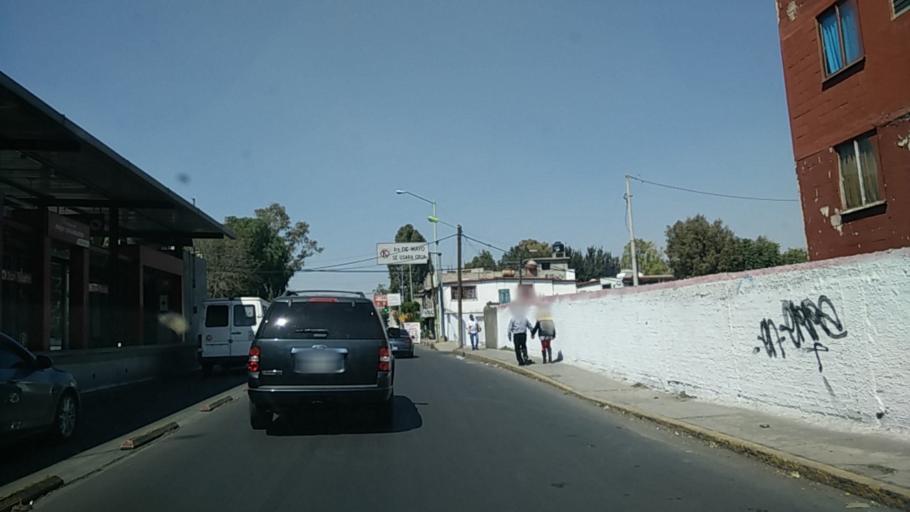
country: MX
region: Mexico
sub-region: Atenco
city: Colonia el Salado
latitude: 19.5958
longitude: -99.0306
